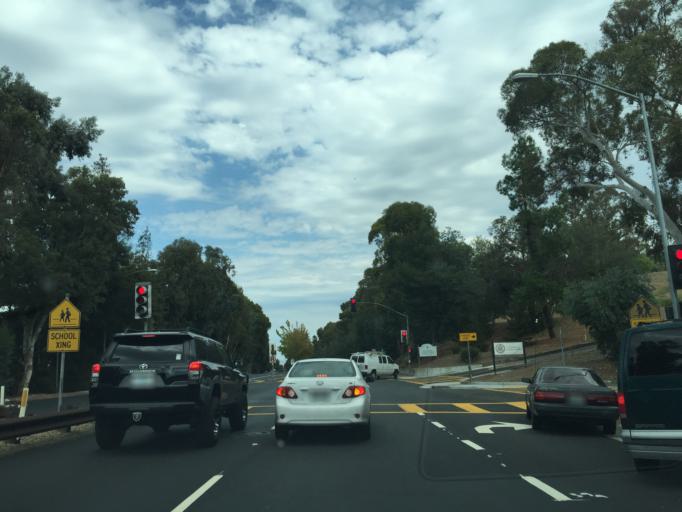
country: US
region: California
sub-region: Santa Clara County
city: Loyola
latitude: 37.3628
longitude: -122.1182
